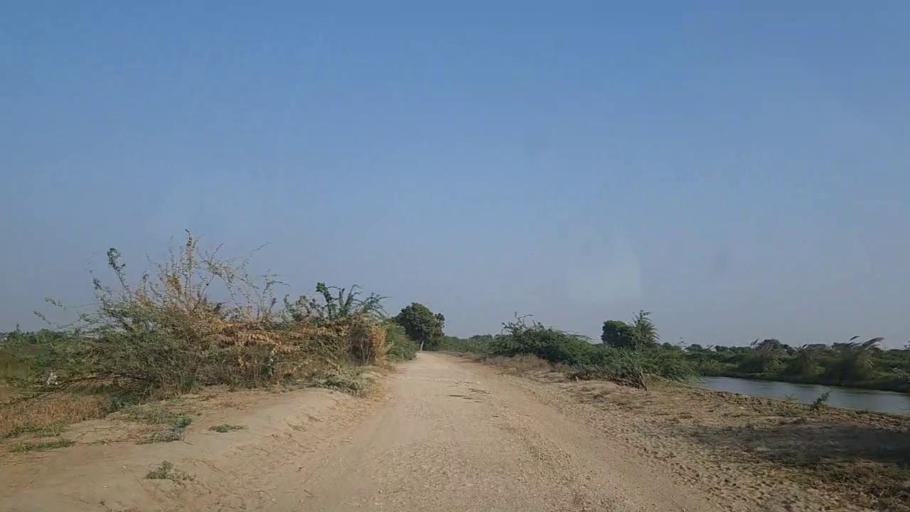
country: PK
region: Sindh
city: Mirpur Sakro
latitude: 24.5747
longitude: 67.6682
